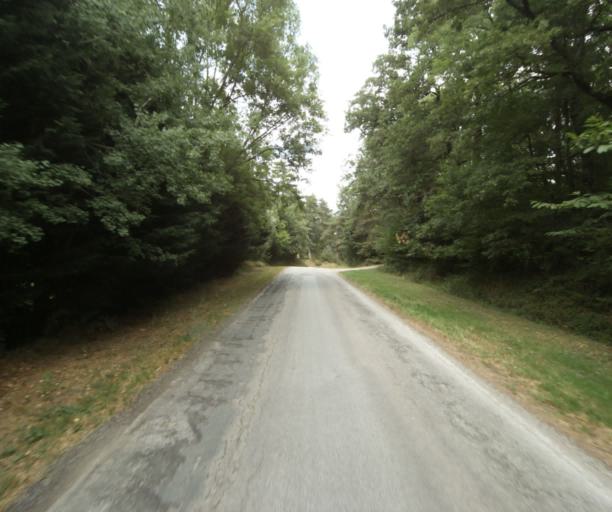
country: FR
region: Midi-Pyrenees
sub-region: Departement de la Haute-Garonne
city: Revel
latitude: 43.4315
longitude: 2.0289
